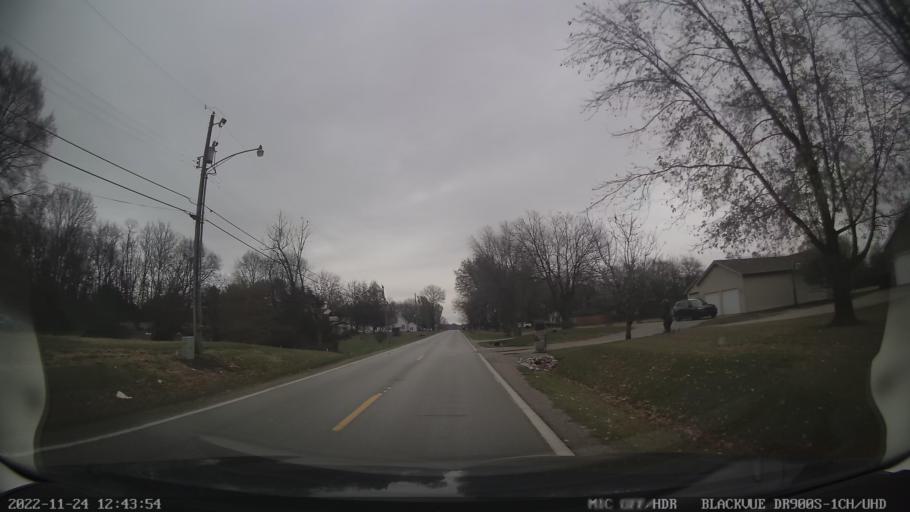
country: US
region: Illinois
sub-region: Macoupin County
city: Staunton
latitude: 38.9614
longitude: -89.7704
